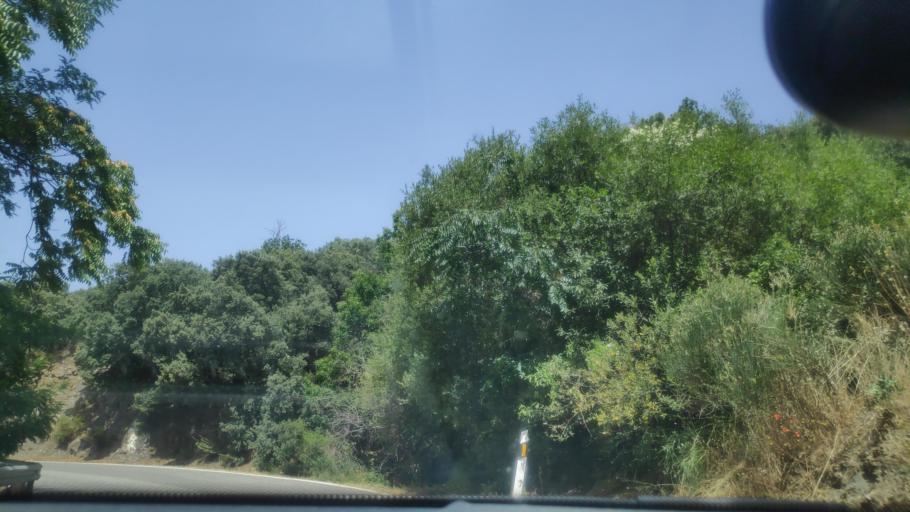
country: ES
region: Andalusia
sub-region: Provincia de Granada
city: Pampaneira
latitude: 36.9317
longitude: -3.3386
